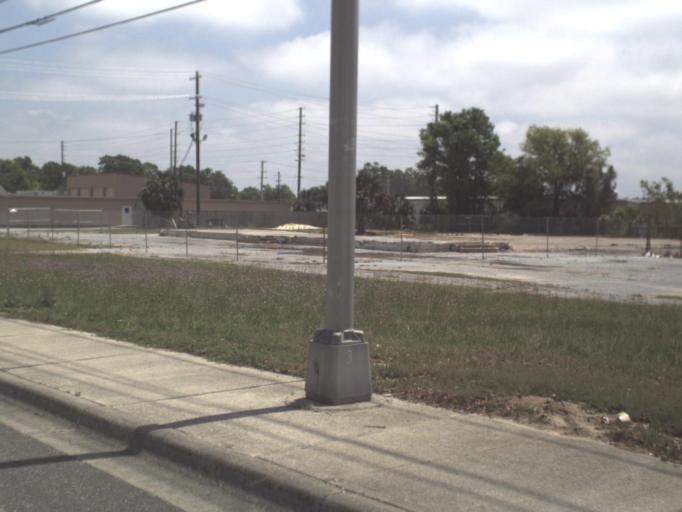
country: US
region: Florida
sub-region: Escambia County
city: Pensacola
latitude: 30.4119
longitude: -87.2439
